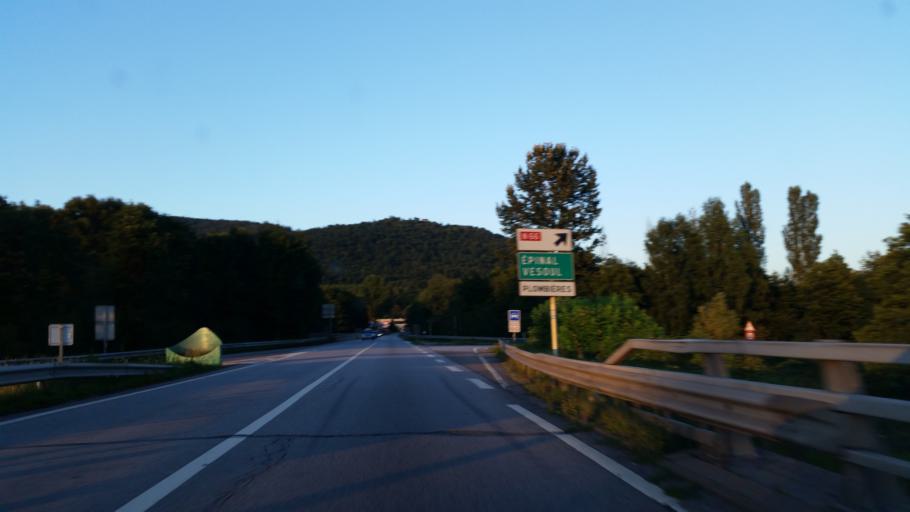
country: FR
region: Lorraine
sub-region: Departement des Vosges
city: Saint-Etienne-les-Remiremont
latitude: 48.0150
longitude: 6.6095
